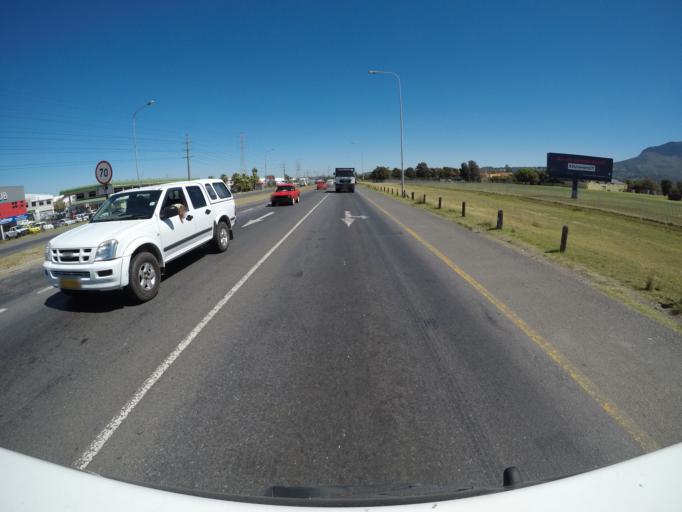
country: ZA
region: Western Cape
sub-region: Cape Winelands District Municipality
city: Stellenbosch
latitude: -34.0956
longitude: 18.8462
